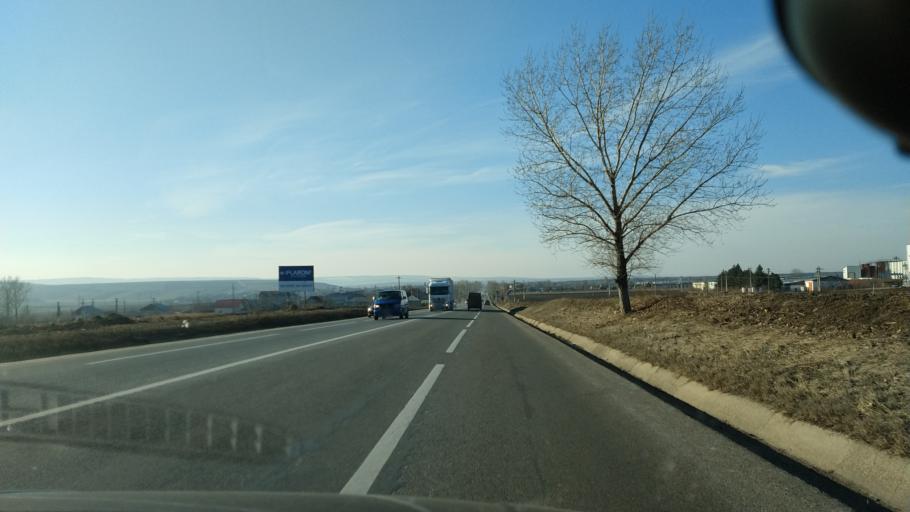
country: RO
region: Iasi
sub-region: Comuna Ion Neculce
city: Razboieni
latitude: 47.2206
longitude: 27.0736
